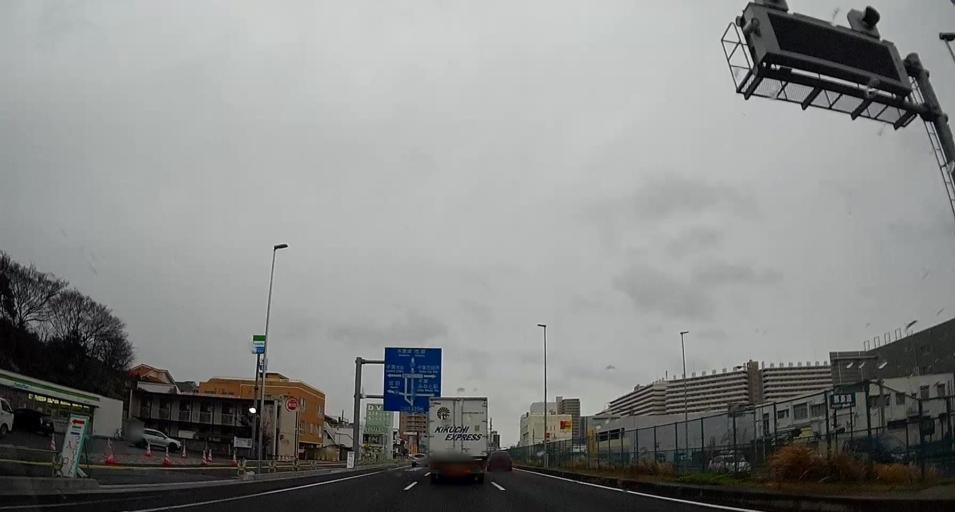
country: JP
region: Chiba
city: Chiba
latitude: 35.6165
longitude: 140.1004
